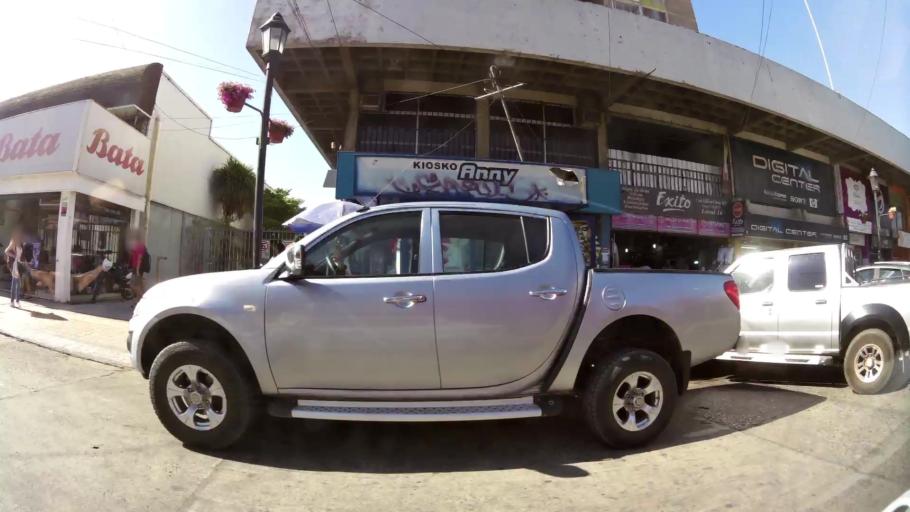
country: CL
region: Maule
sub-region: Provincia de Talca
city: Talca
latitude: -35.4281
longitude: -71.6533
